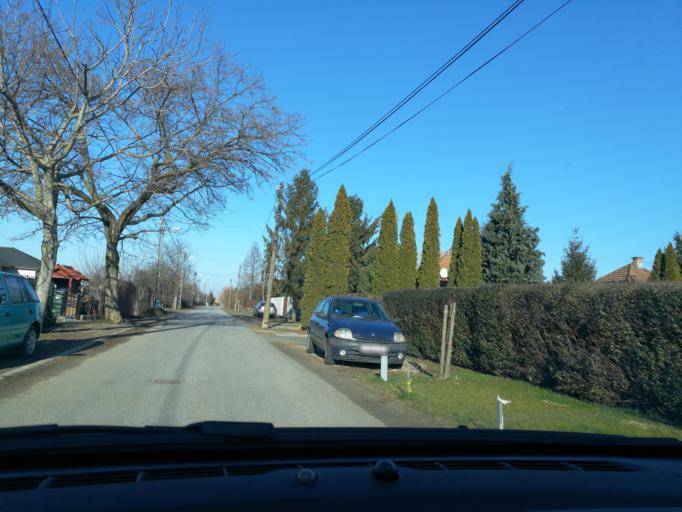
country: HU
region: Szabolcs-Szatmar-Bereg
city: Nyiregyhaza
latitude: 47.9470
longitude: 21.7528
